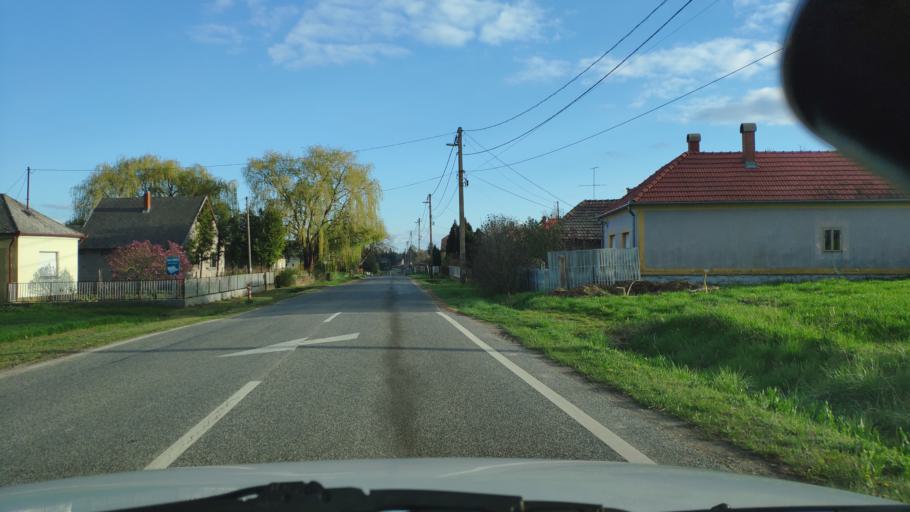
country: HU
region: Zala
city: Zalakomar
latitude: 46.4917
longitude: 17.1279
